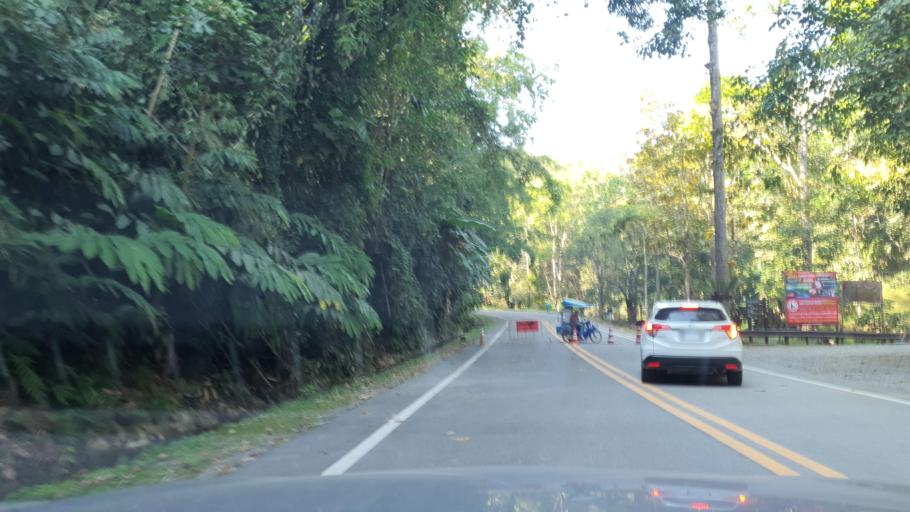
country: TH
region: Chiang Rai
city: Mae Lao
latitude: 19.8755
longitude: 99.6262
